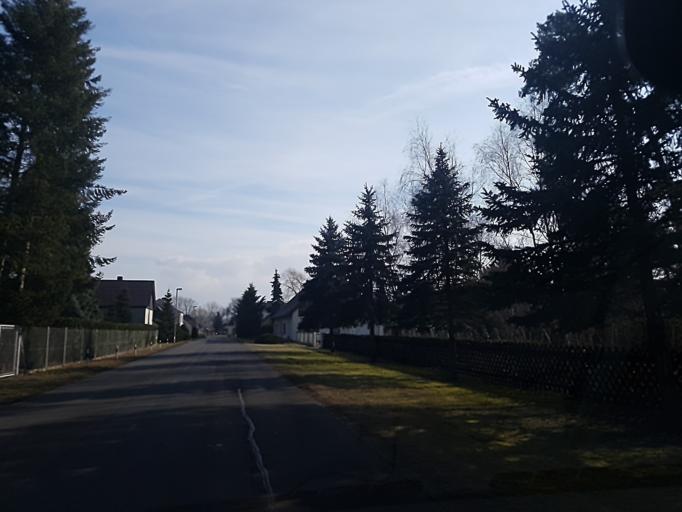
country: DE
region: Brandenburg
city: Wenzlow
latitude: 52.3043
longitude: 12.4440
